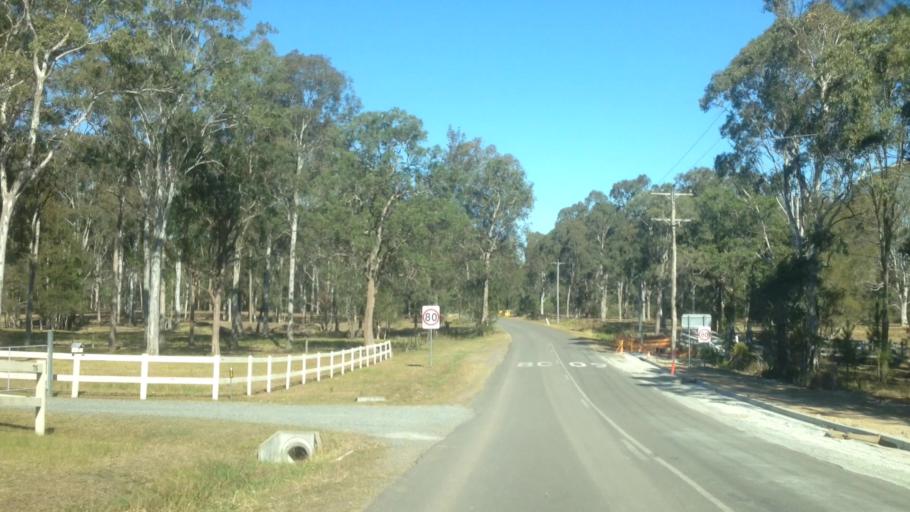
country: AU
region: New South Wales
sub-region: Lake Macquarie Shire
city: Cooranbong
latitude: -33.0941
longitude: 151.4517
